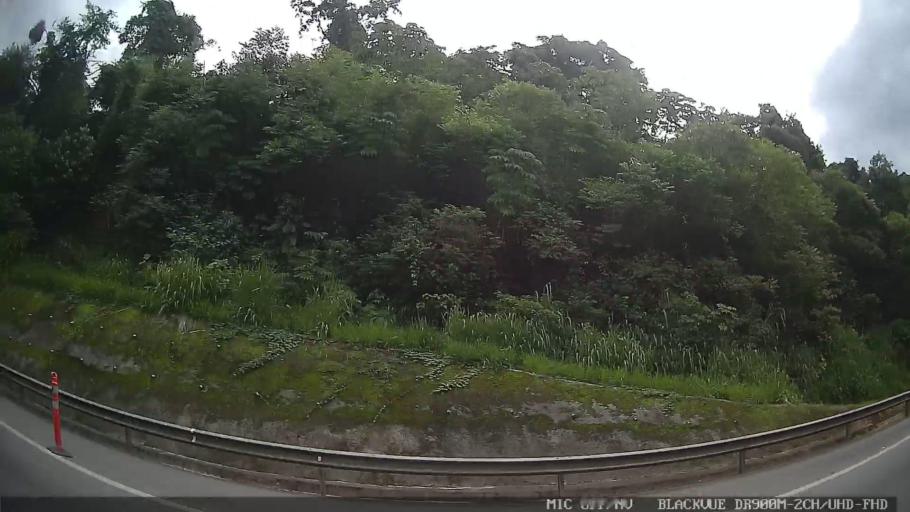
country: BR
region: Sao Paulo
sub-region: Cubatao
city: Cubatao
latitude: -23.9320
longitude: -46.4643
